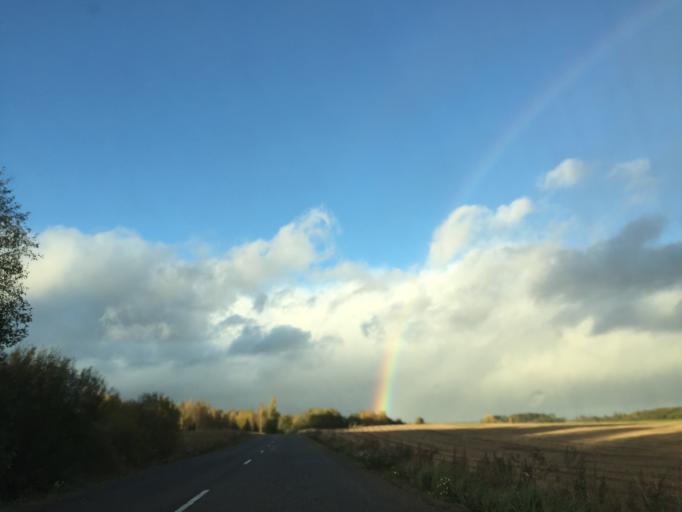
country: LV
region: Broceni
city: Broceni
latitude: 56.8908
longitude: 22.3942
